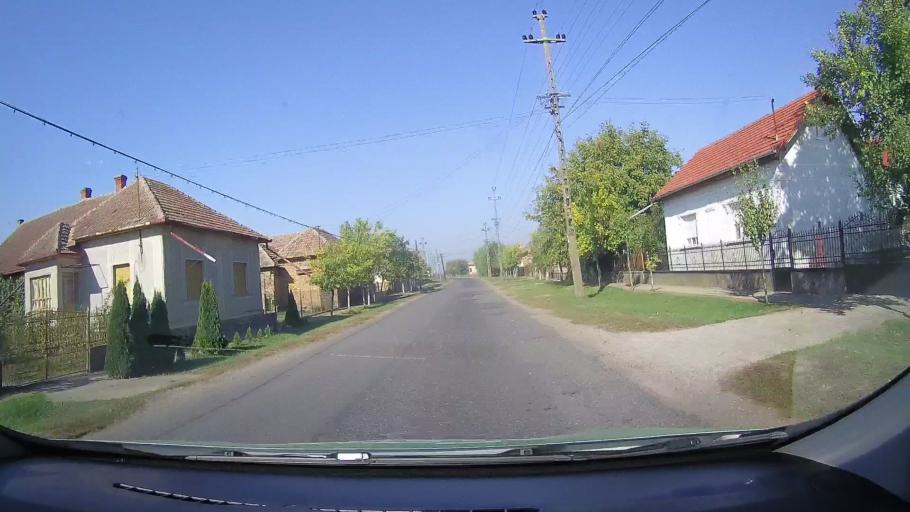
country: RO
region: Satu Mare
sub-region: Comuna Petresti
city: Petresti
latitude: 47.6077
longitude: 22.3588
